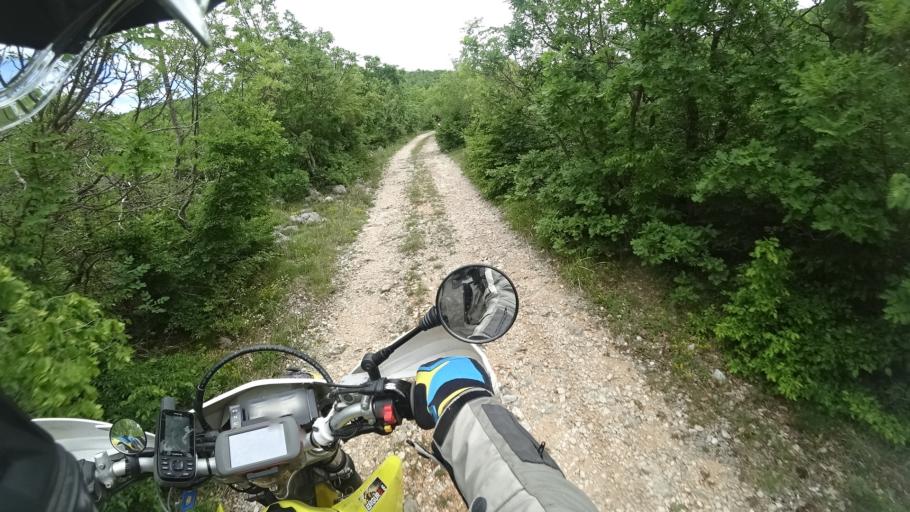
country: HR
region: Splitsko-Dalmatinska
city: Hrvace
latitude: 43.8936
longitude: 16.5374
